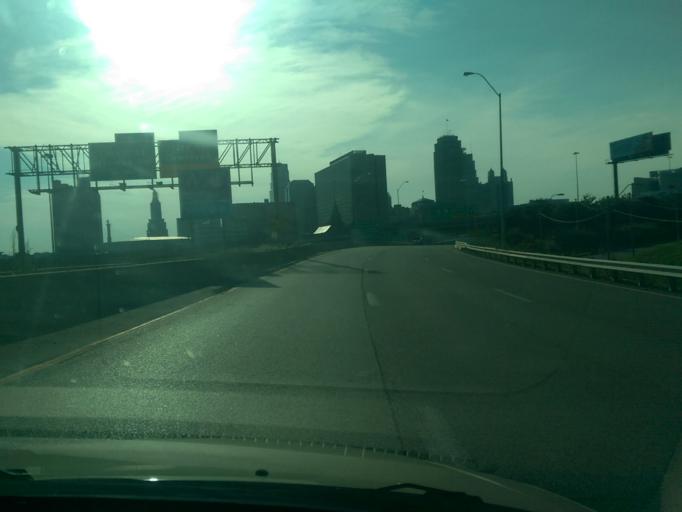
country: US
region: Missouri
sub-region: Jackson County
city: Kansas City
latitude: 39.0966
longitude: -94.5691
